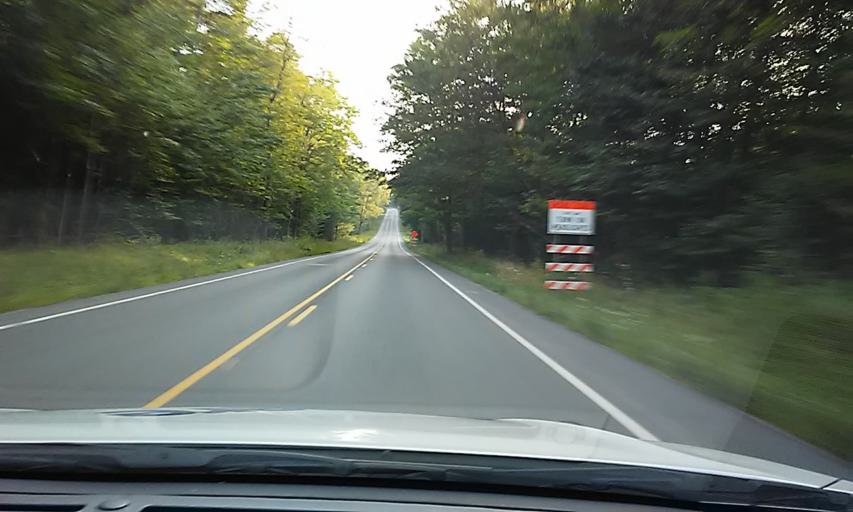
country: US
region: Pennsylvania
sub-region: McKean County
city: Kane
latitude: 41.5793
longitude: -78.8699
